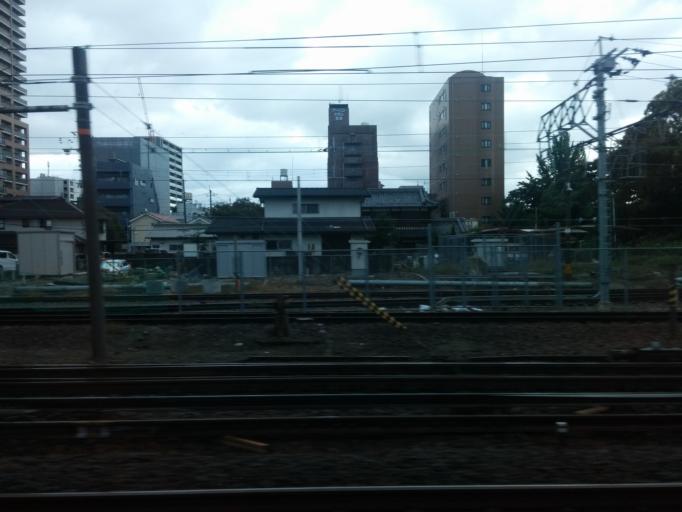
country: JP
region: Shiga Prefecture
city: Kusatsu
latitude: 35.0200
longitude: 135.9594
